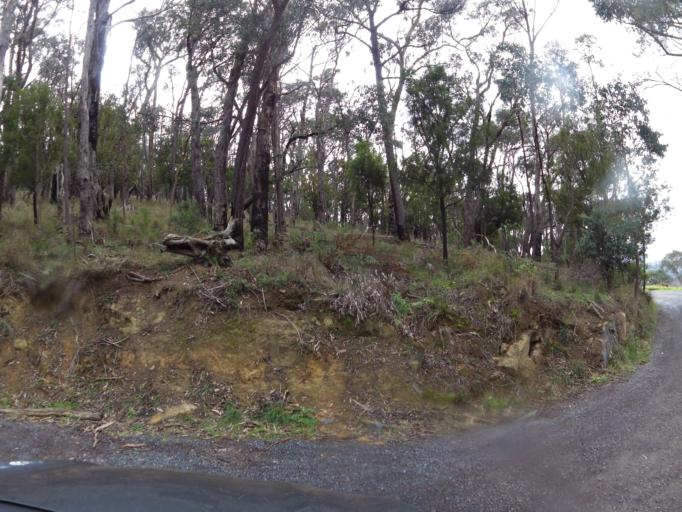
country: AU
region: Victoria
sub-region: Knox
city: The Basin
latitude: -37.8629
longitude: 145.3168
